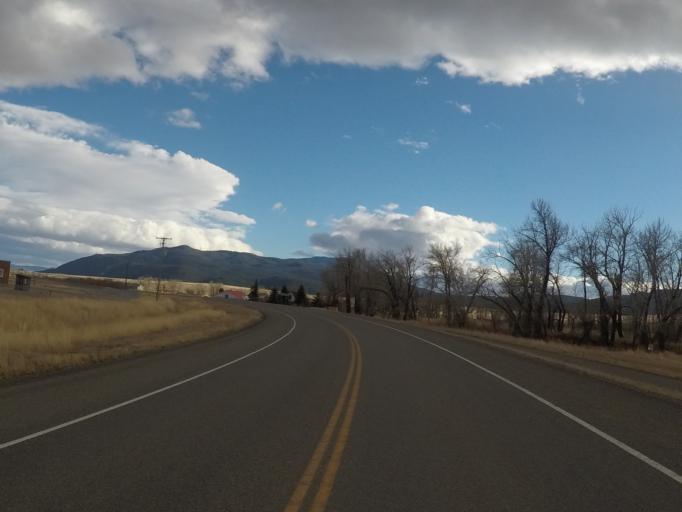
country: US
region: Montana
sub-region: Jefferson County
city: Boulder
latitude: 46.2277
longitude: -112.1223
